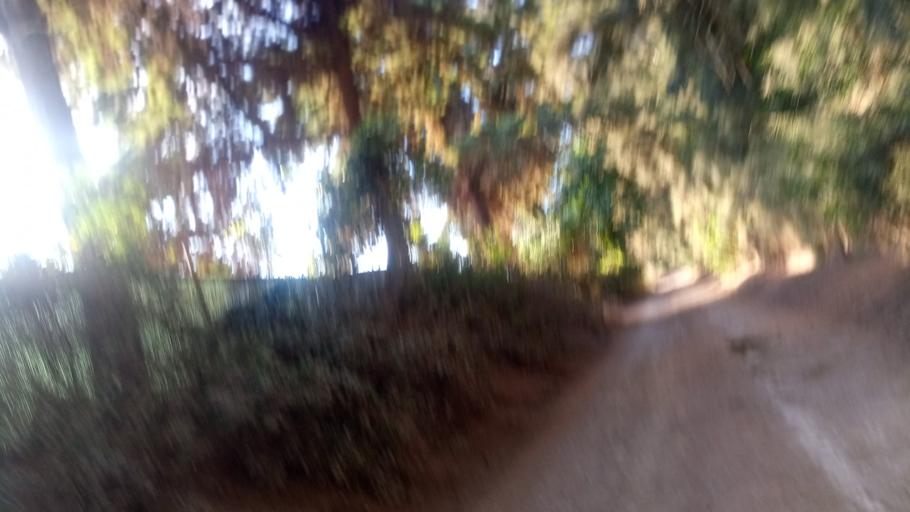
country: PT
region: Faro
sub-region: Tavira
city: Tavira
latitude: 37.1526
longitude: -7.5741
